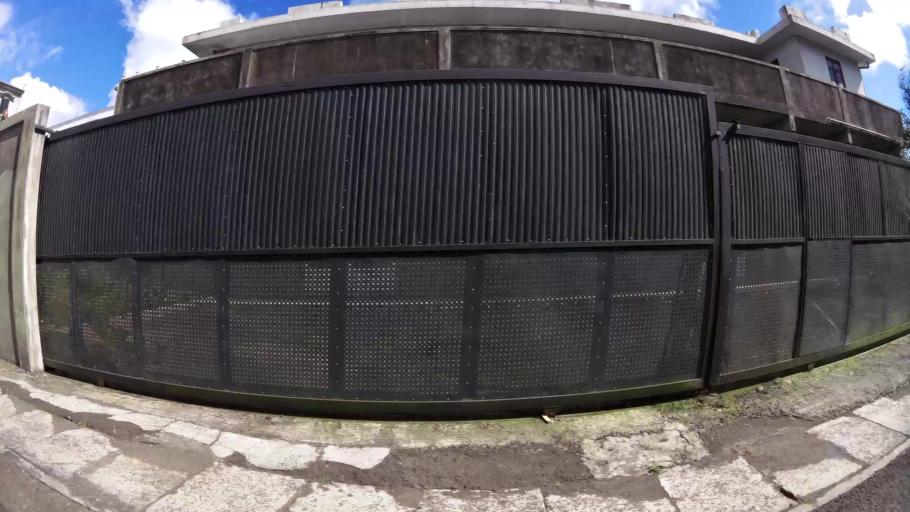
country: MU
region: Plaines Wilhems
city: Curepipe
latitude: -20.3293
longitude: 57.5313
